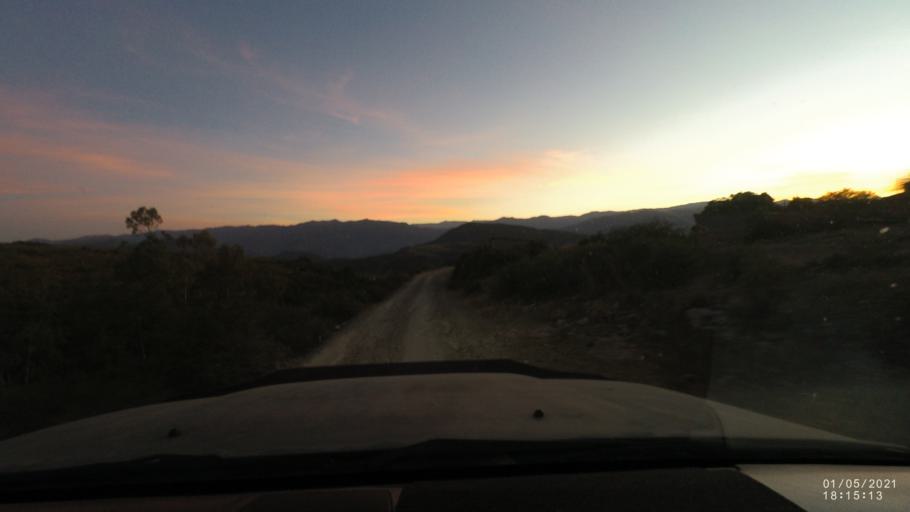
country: BO
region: Cochabamba
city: Capinota
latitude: -17.6738
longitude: -66.2147
